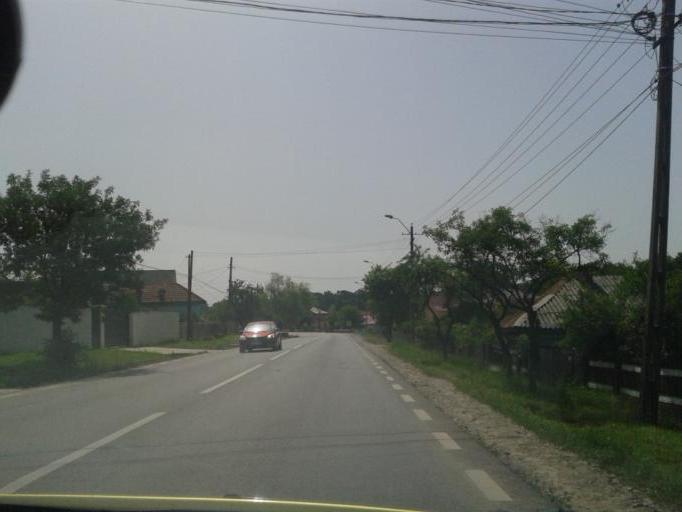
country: RO
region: Arges
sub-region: Comuna Babana
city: Babana
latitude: 44.8956
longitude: 24.7413
